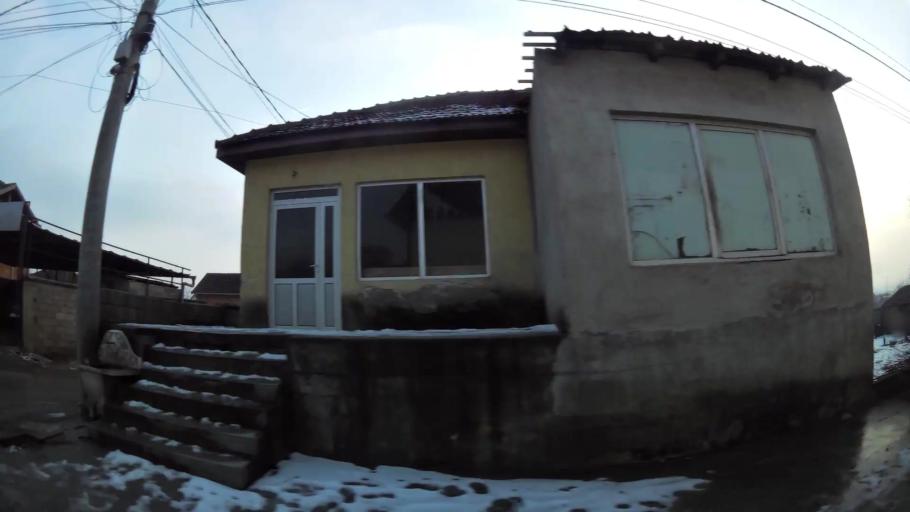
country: MK
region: Aracinovo
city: Arachinovo
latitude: 42.0228
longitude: 21.5643
